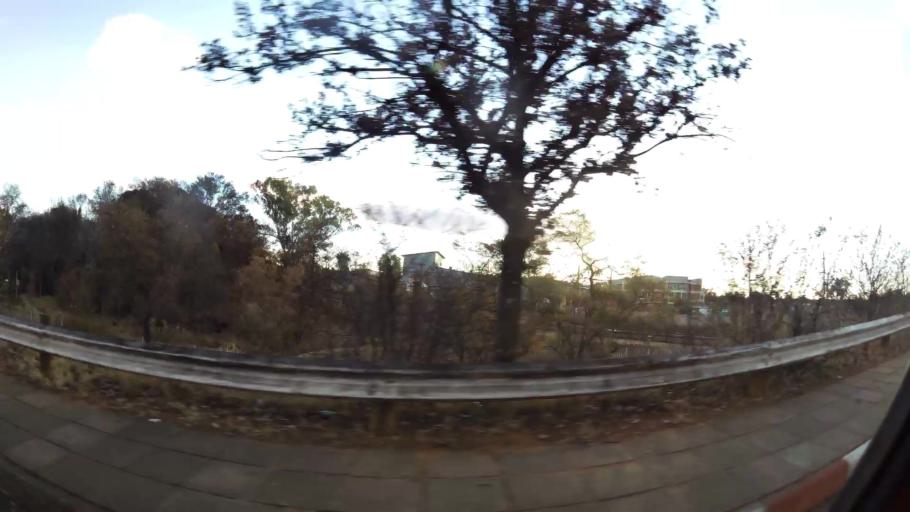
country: ZA
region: North-West
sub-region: Dr Kenneth Kaunda District Municipality
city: Potchefstroom
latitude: -26.6808
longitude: 27.0959
